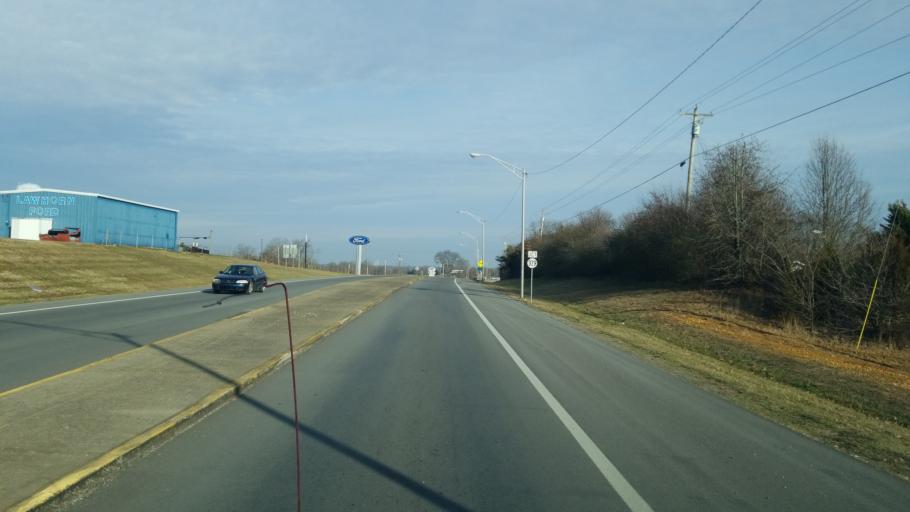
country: US
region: Kentucky
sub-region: Russell County
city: Russell Springs
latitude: 37.0668
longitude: -85.0713
